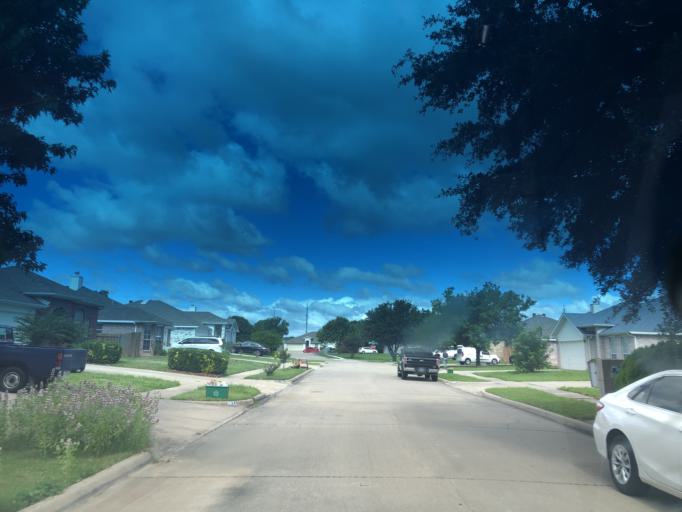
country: US
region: Texas
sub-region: Dallas County
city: Grand Prairie
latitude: 32.6953
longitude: -97.0300
